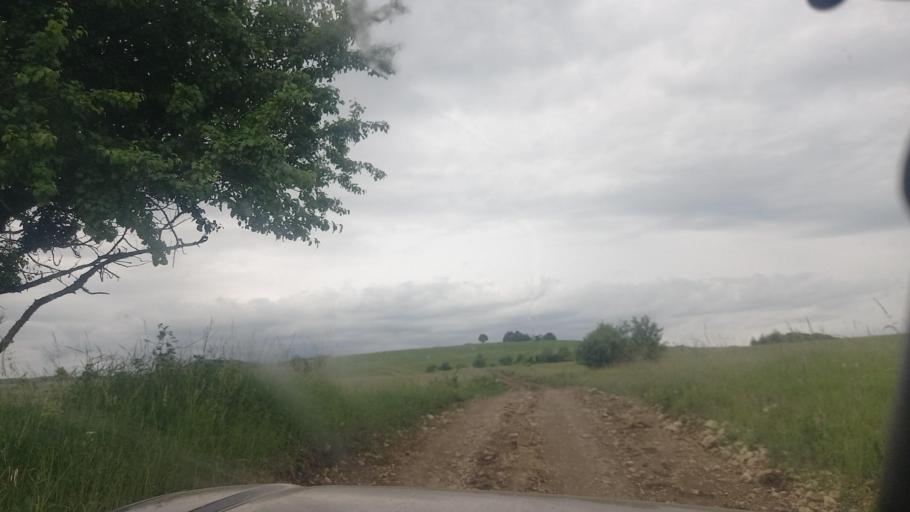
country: RU
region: Krasnodarskiy
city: Peredovaya
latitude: 44.0731
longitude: 41.3643
